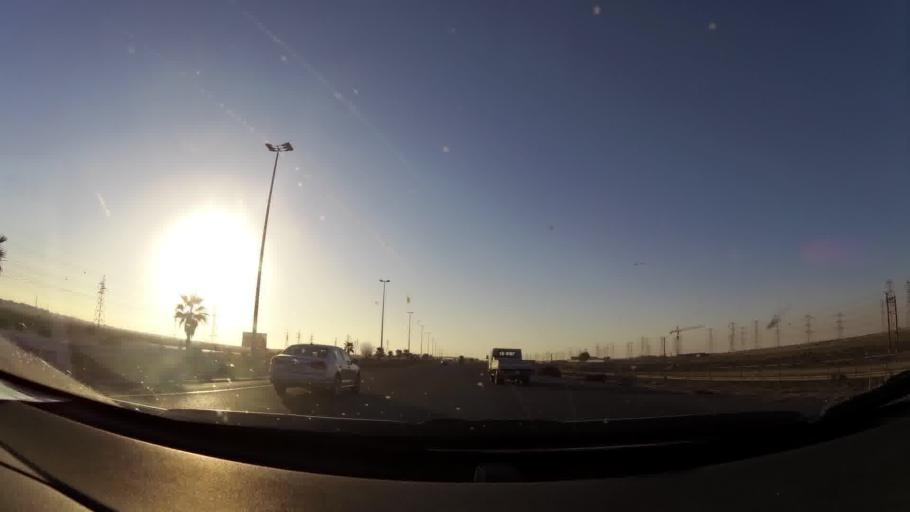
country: KW
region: Al Ahmadi
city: Al Fahahil
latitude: 28.8956
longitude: 48.2212
